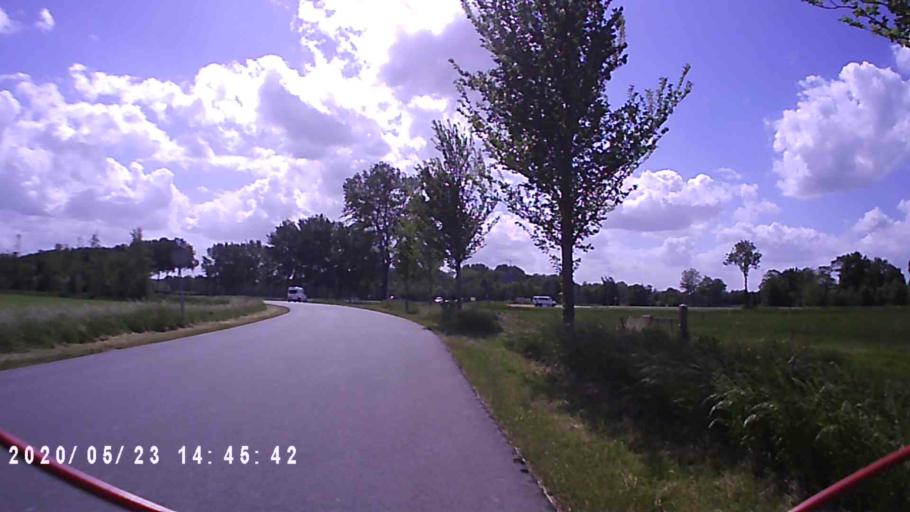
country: NL
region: Groningen
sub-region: Gemeente Delfzijl
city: Delfzijl
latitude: 53.2637
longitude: 6.9529
